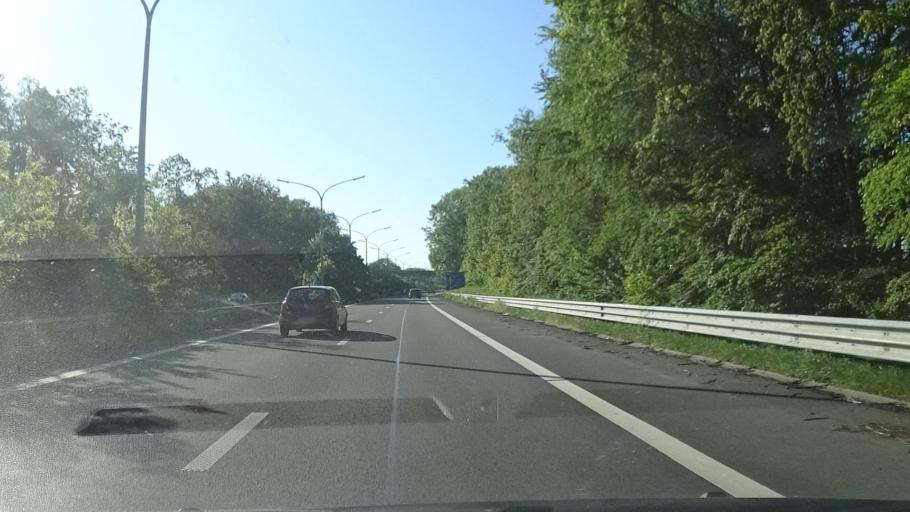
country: BE
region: Wallonia
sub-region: Province du Hainaut
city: La Louviere
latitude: 50.5159
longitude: 4.2040
